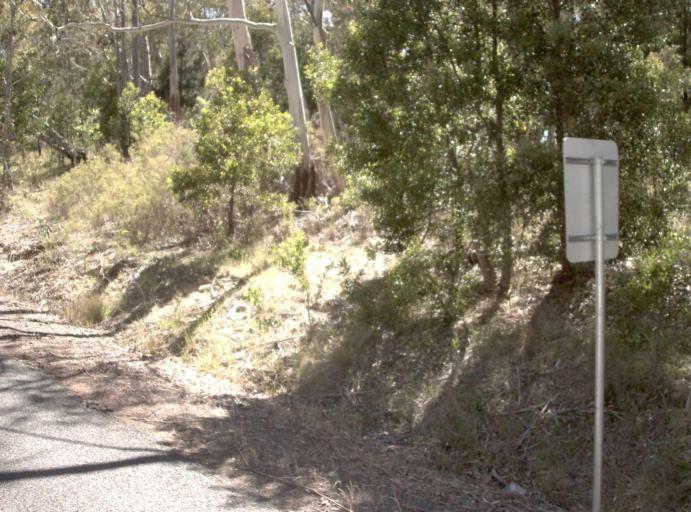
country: AU
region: New South Wales
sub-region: Bombala
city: Bombala
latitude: -37.0586
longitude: 148.8025
